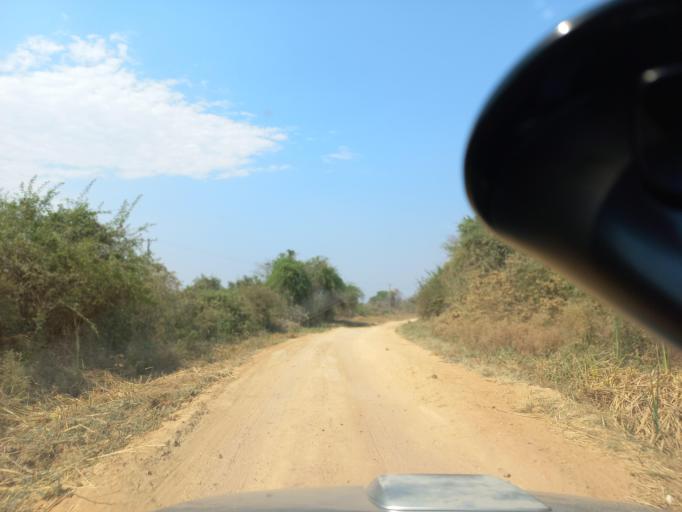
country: ZW
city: Chirundu
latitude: -15.9263
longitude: 28.8741
